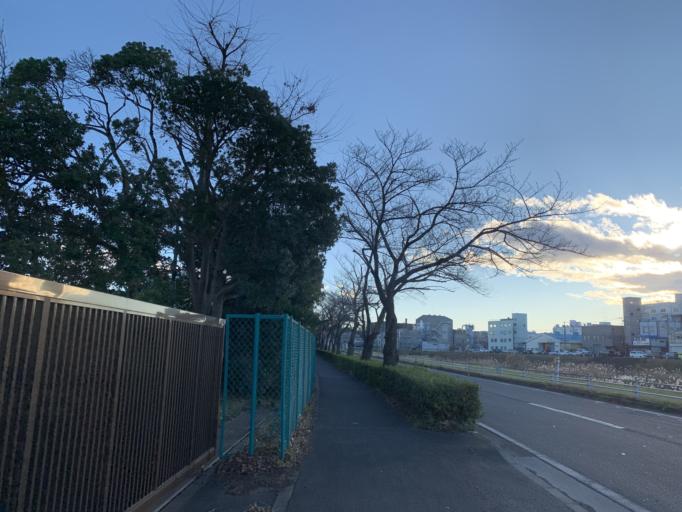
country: JP
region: Tokyo
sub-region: Machida-shi
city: Machida
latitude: 35.5168
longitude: 139.5520
